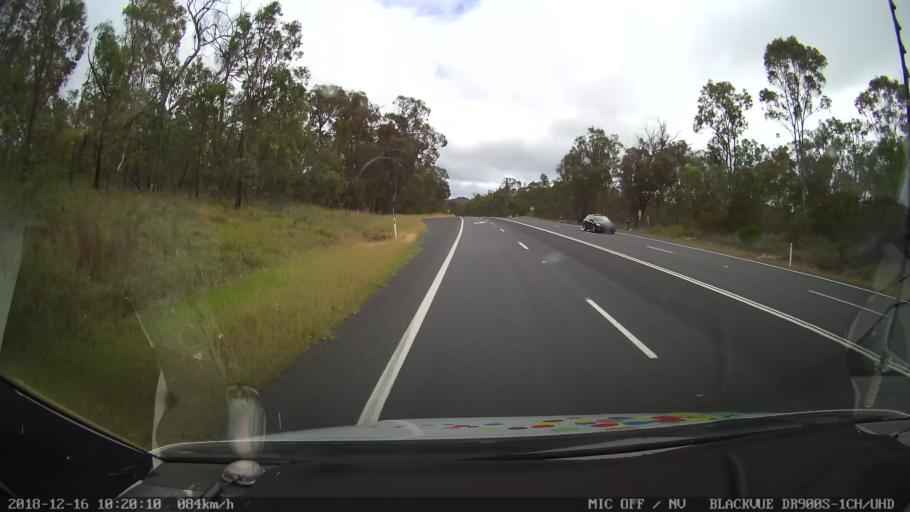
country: AU
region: New South Wales
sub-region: Tenterfield Municipality
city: Carrolls Creek
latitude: -29.2236
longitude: 152.0096
